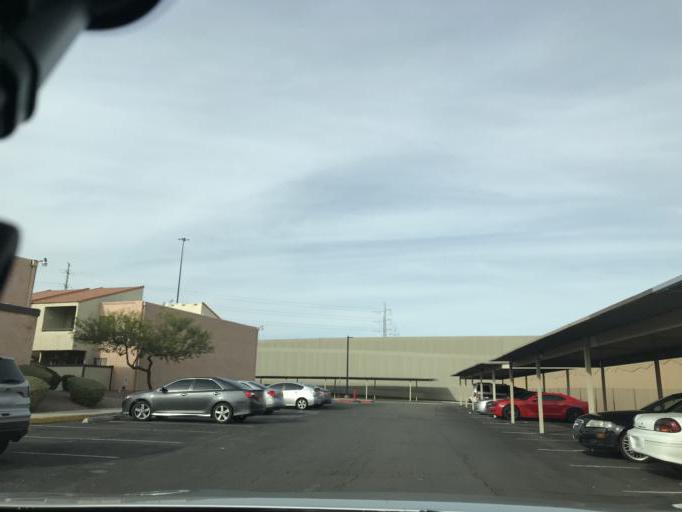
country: US
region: Nevada
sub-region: Clark County
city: Las Vegas
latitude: 36.1744
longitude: -115.1625
